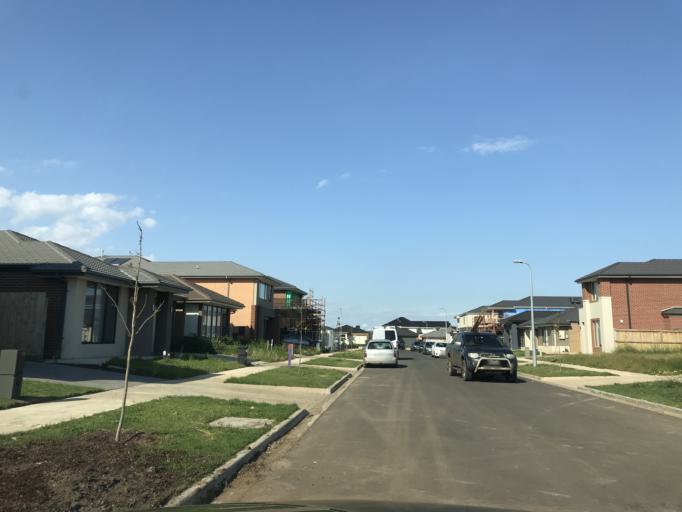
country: AU
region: Victoria
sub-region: Wyndham
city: Hoppers Crossing
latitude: -37.8910
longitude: 144.7122
